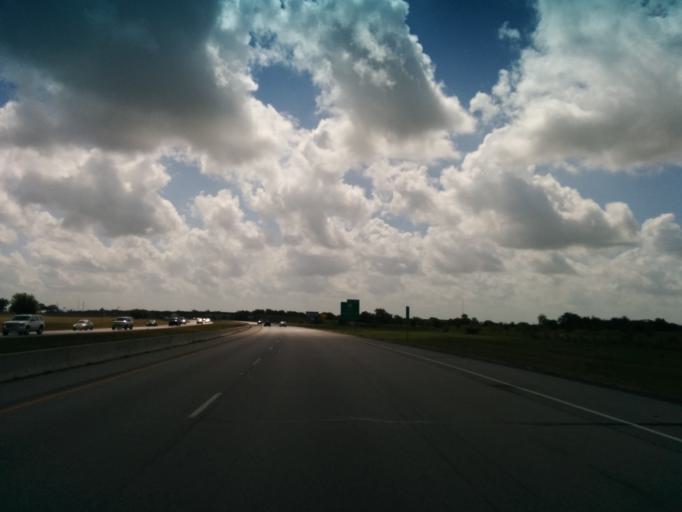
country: US
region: Texas
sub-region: Austin County
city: Sealy
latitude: 29.7602
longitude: -96.1761
